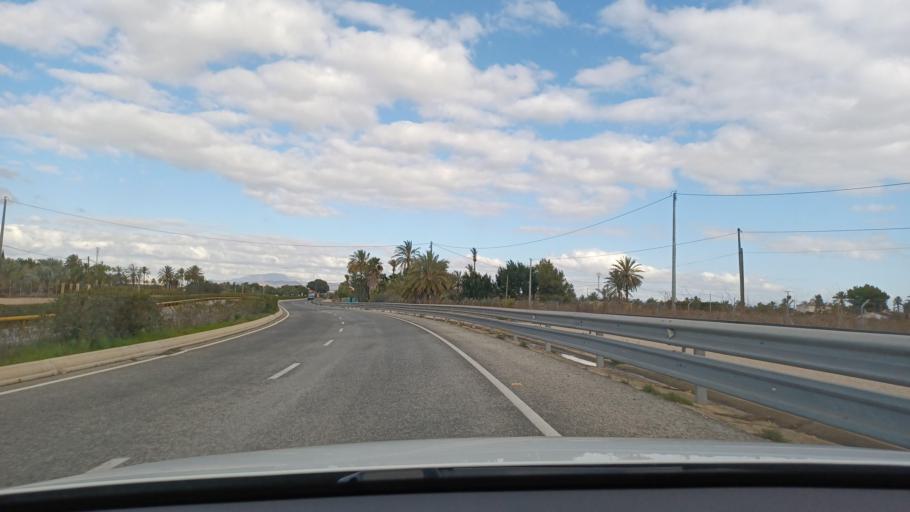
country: ES
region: Valencia
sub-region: Provincia de Alicante
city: Elche
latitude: 38.2086
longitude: -0.6974
